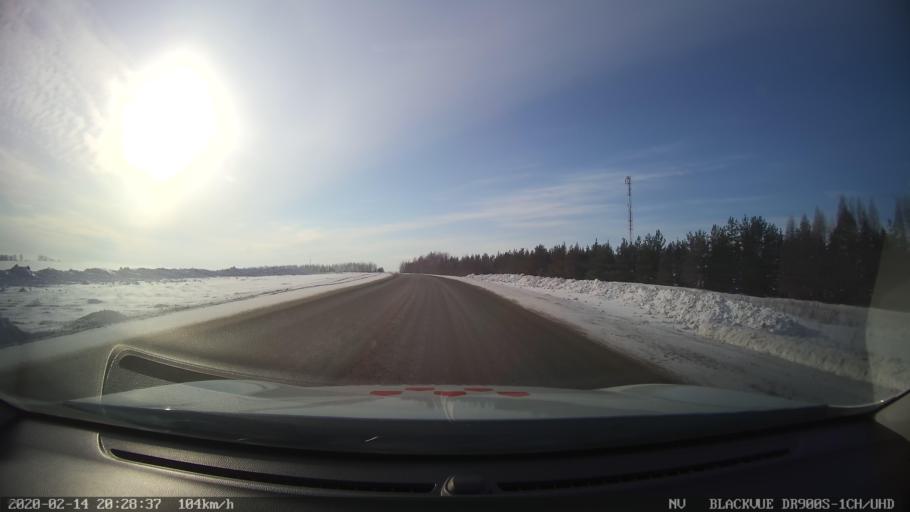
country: RU
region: Tatarstan
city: Stolbishchi
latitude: 55.4608
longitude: 48.9776
